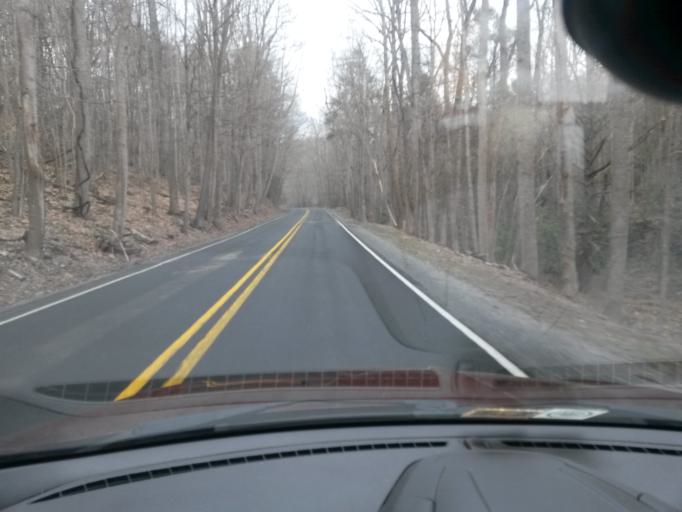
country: US
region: Virginia
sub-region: Bath County
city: Warm Springs
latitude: 38.1595
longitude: -79.7359
